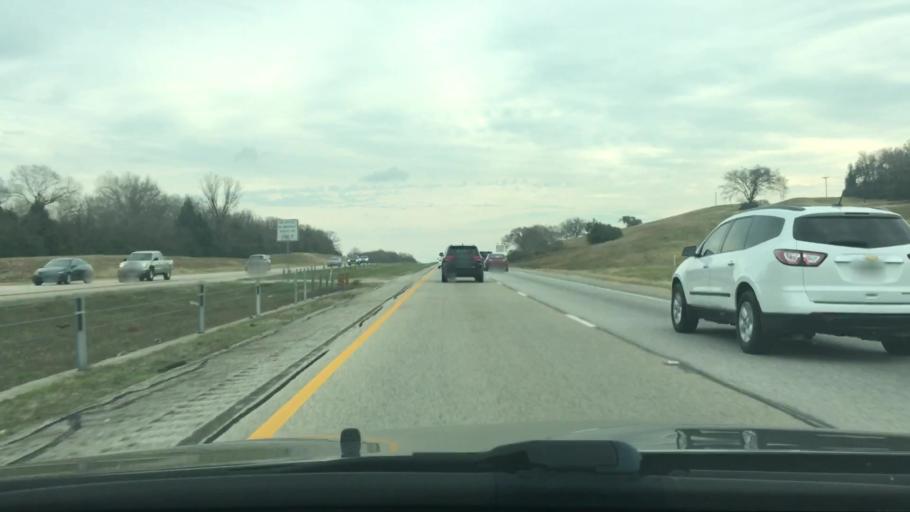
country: US
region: Texas
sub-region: Leon County
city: Centerville
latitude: 31.2906
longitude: -95.9963
